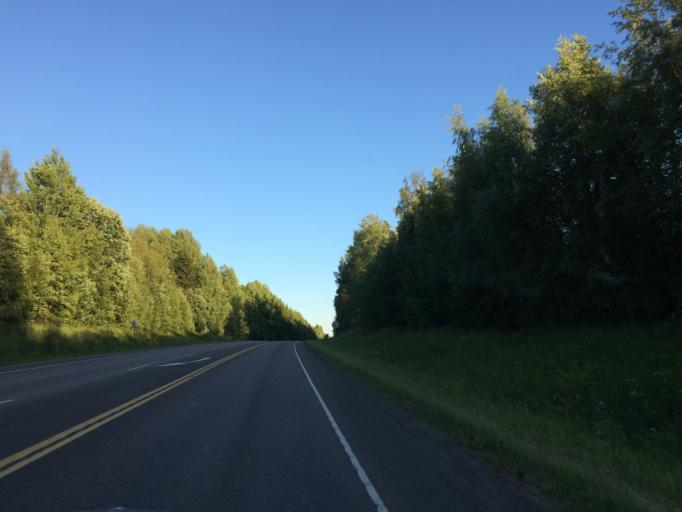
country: FI
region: Haeme
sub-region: Riihimaeki
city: Riihimaeki
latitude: 60.7631
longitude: 24.7137
